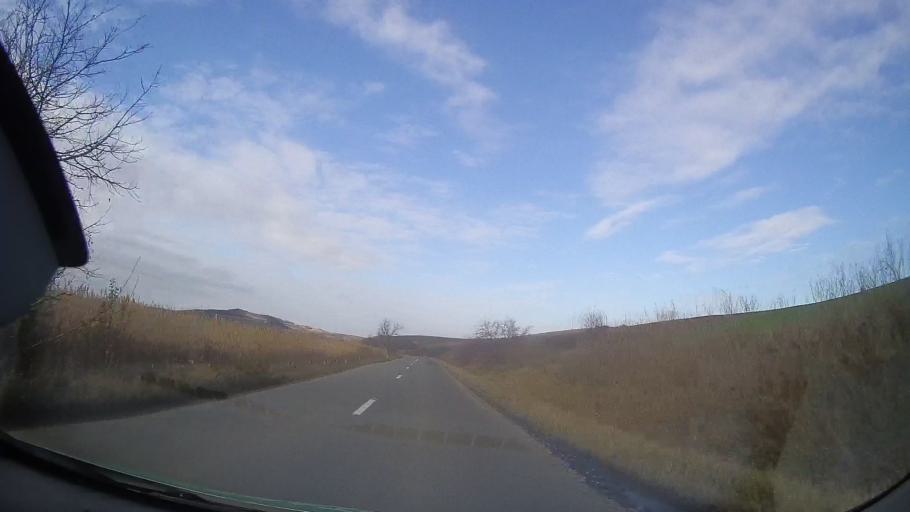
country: RO
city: Barza
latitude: 46.5635
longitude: 24.0975
